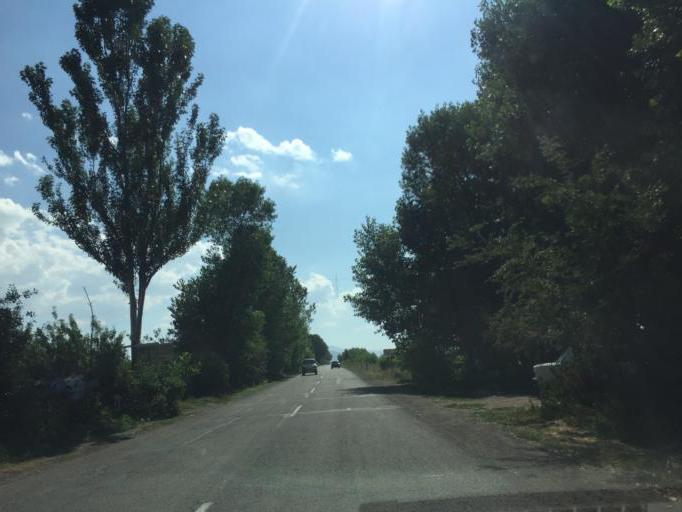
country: AM
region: Geghark'unik'i Marz
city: Tsovinar
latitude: 40.1605
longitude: 45.4569
